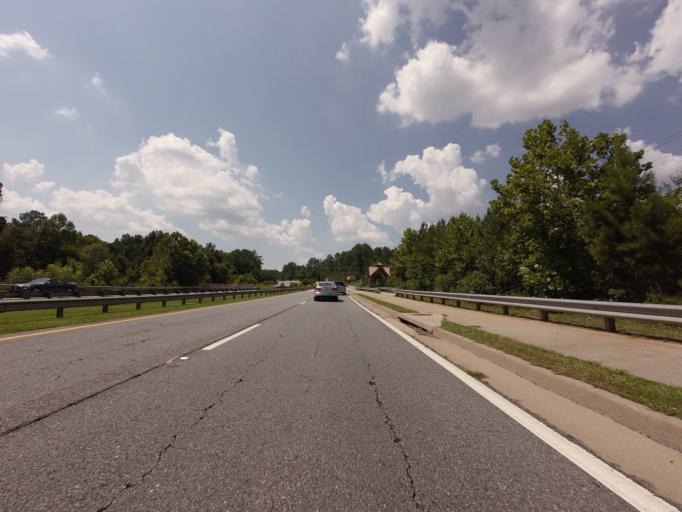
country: US
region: Georgia
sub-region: Fulton County
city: Johns Creek
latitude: 34.0266
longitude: -84.2020
